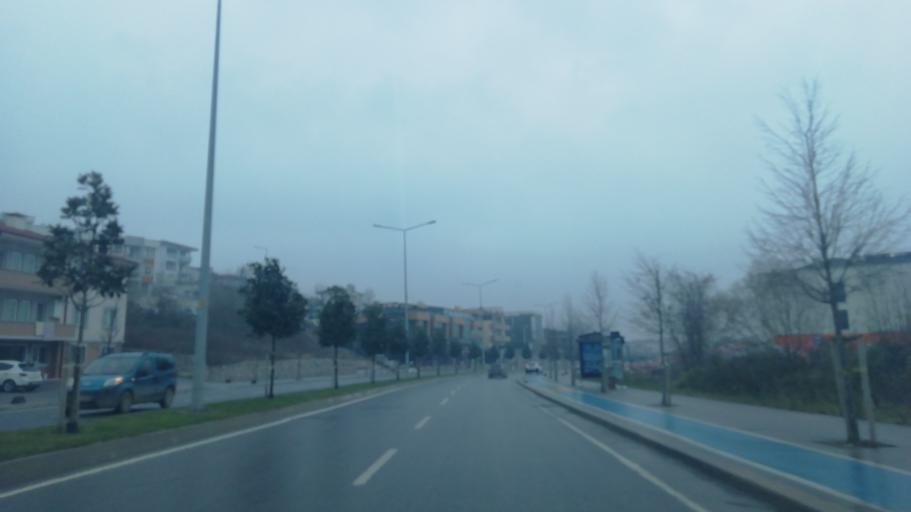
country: TR
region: Sakarya
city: Adapazari
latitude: 40.7586
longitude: 30.3518
